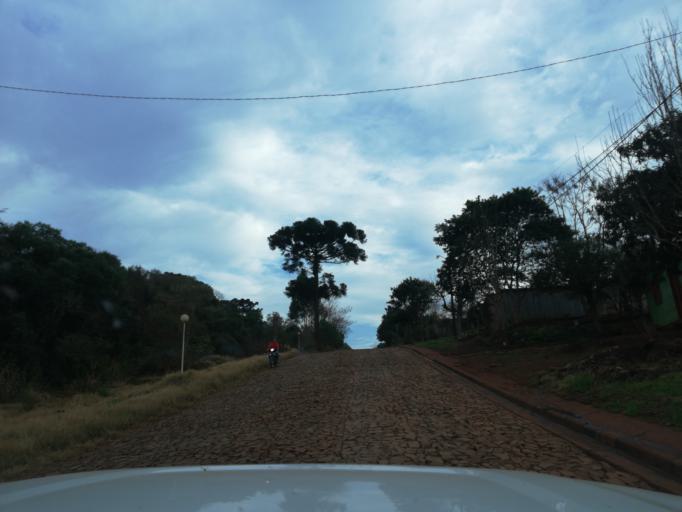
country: AR
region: Misiones
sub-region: Departamento de San Pedro
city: San Pedro
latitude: -26.6275
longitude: -54.0945
